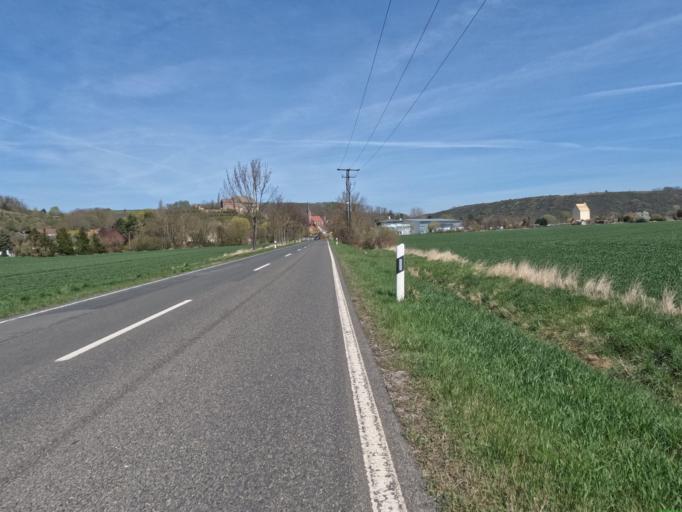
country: DE
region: Saxony-Anhalt
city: Beesenstedt
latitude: 51.6159
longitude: 11.7401
